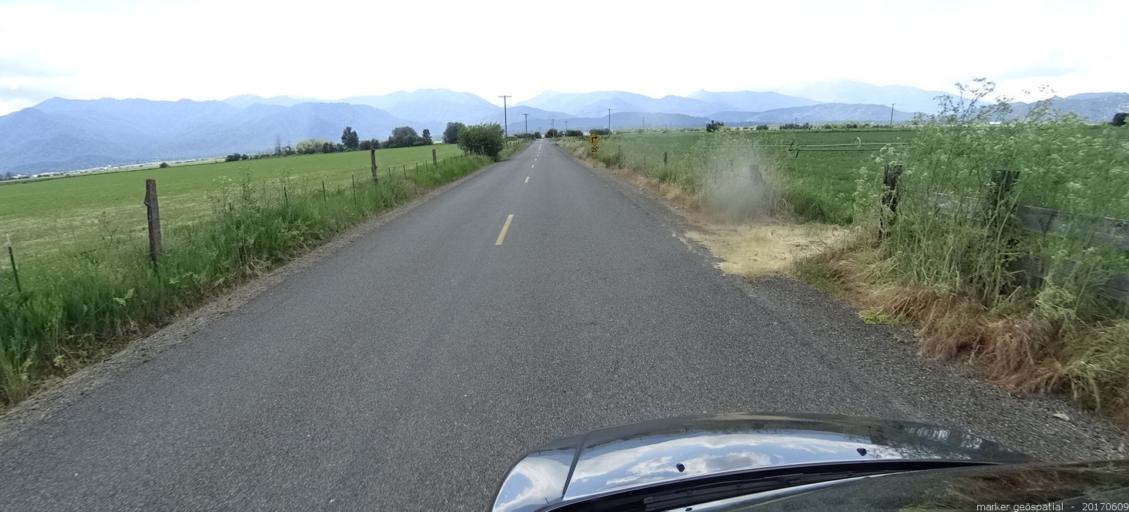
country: US
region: California
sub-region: Siskiyou County
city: Yreka
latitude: 41.5194
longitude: -122.8557
